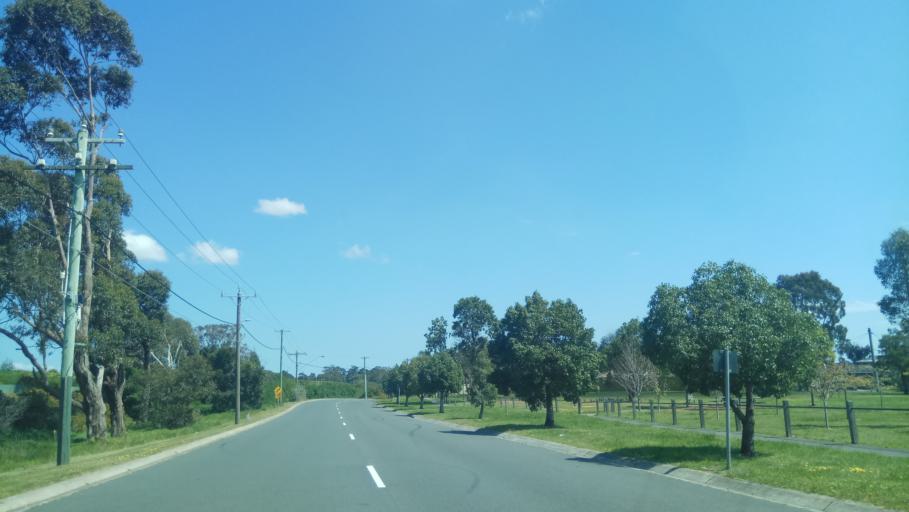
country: AU
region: Victoria
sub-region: Greater Dandenong
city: Springvale South
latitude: -37.9676
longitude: 145.1390
